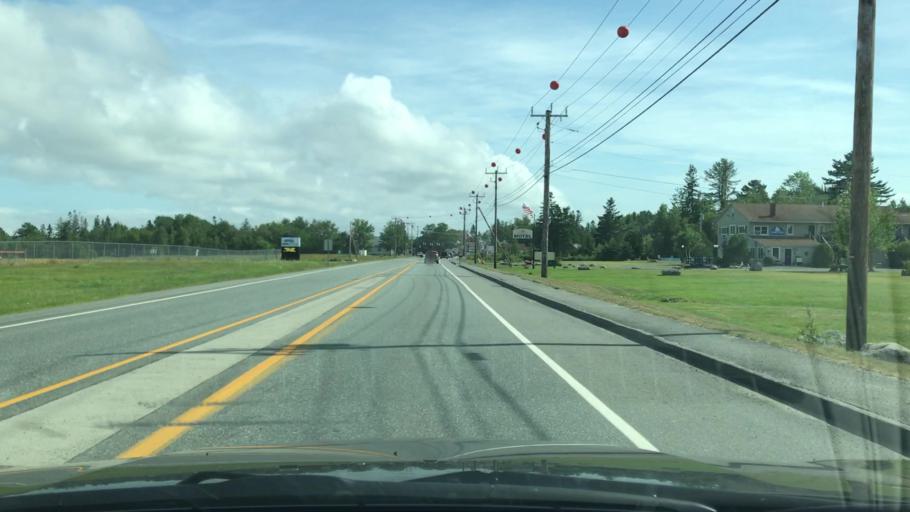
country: US
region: Maine
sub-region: Hancock County
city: Trenton
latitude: 44.4430
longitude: -68.3699
